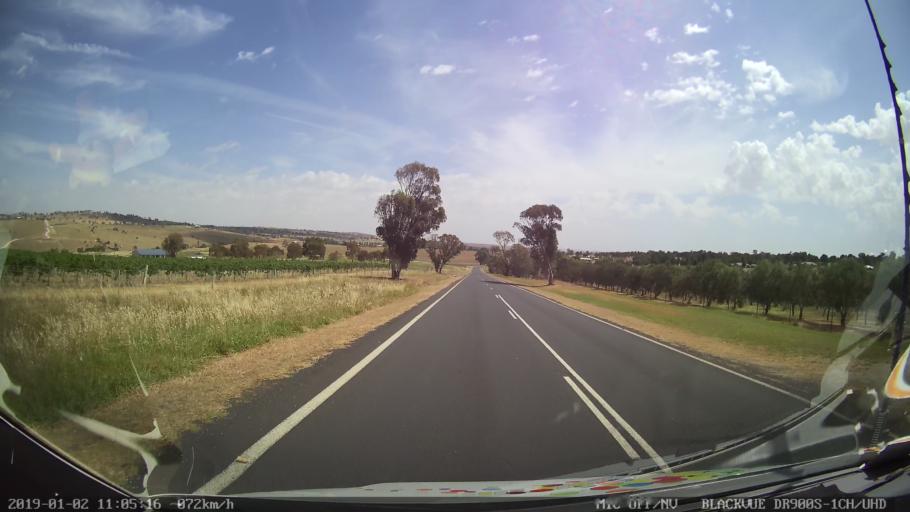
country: AU
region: New South Wales
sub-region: Young
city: Young
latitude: -34.5668
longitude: 148.3541
